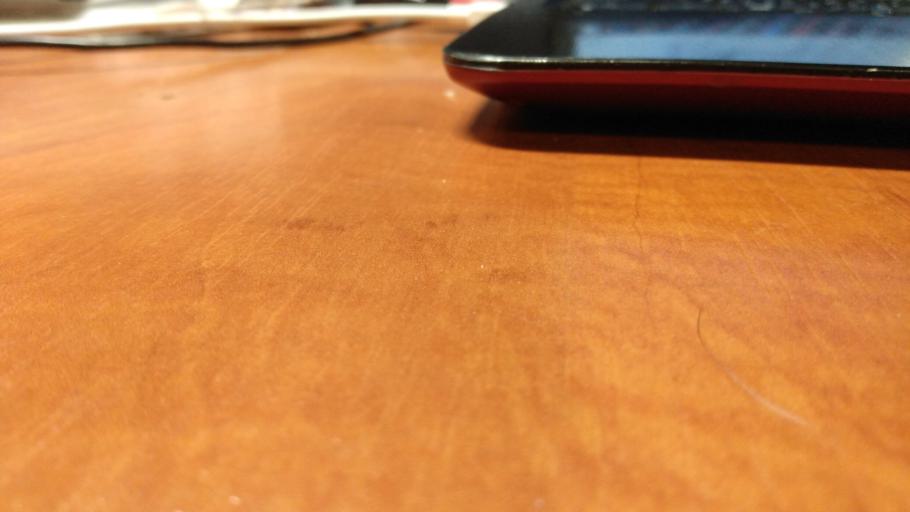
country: RU
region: Vologda
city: Babayevo
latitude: 59.1265
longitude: 36.1838
